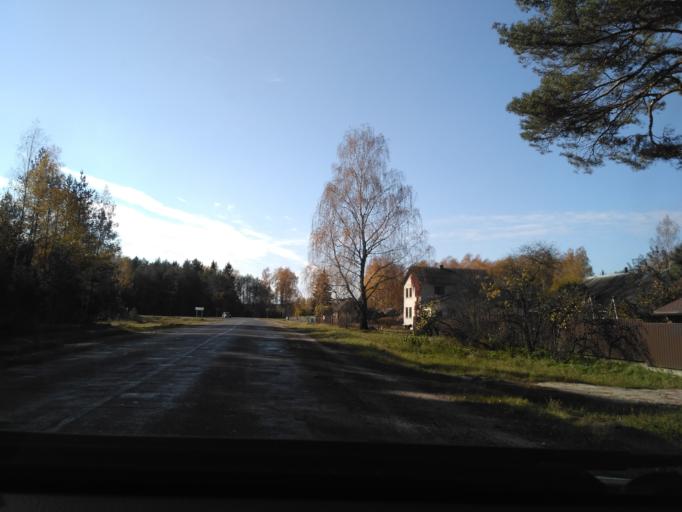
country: BY
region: Minsk
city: Horad Barysaw
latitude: 54.2569
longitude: 28.5741
